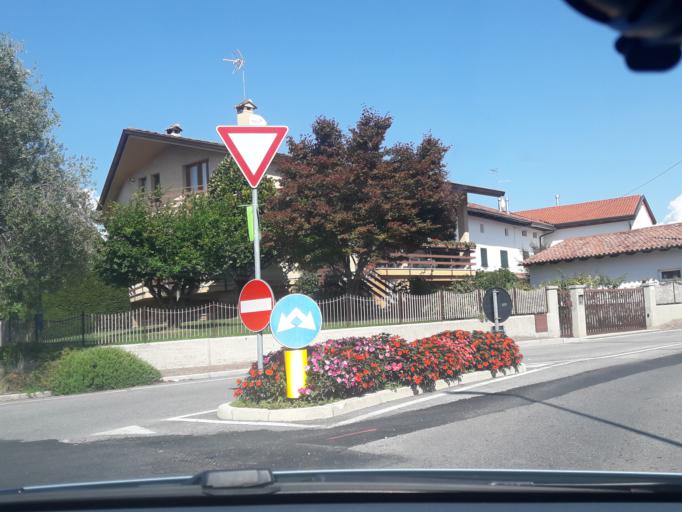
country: IT
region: Friuli Venezia Giulia
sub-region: Provincia di Udine
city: Colugna
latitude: 46.1011
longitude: 13.2093
